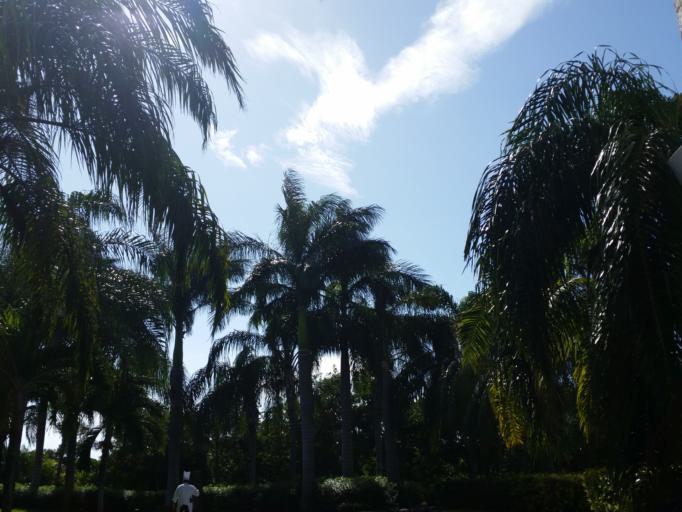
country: MX
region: Quintana Roo
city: Playa del Carmen
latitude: 20.6685
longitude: -87.0300
